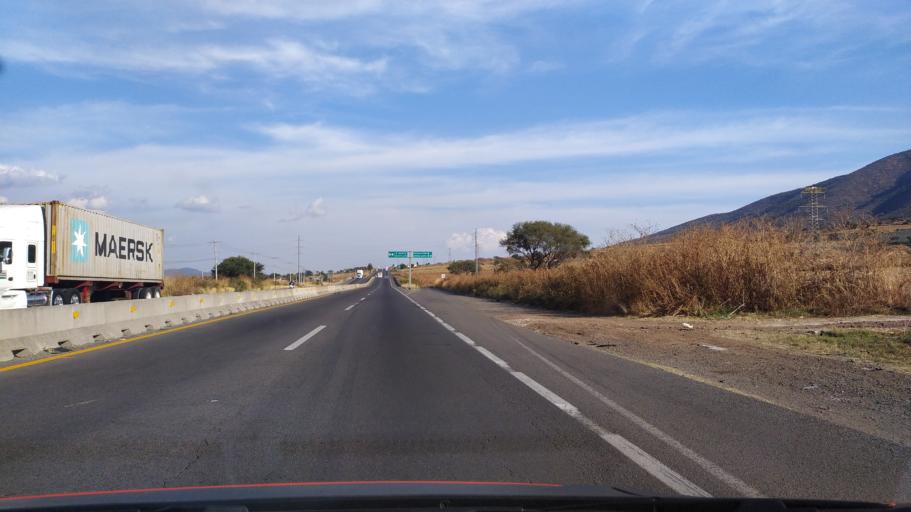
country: MX
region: Jalisco
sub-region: Poncitlan
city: El Romereno (INFONAVIT)
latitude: 20.3958
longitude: -103.0245
